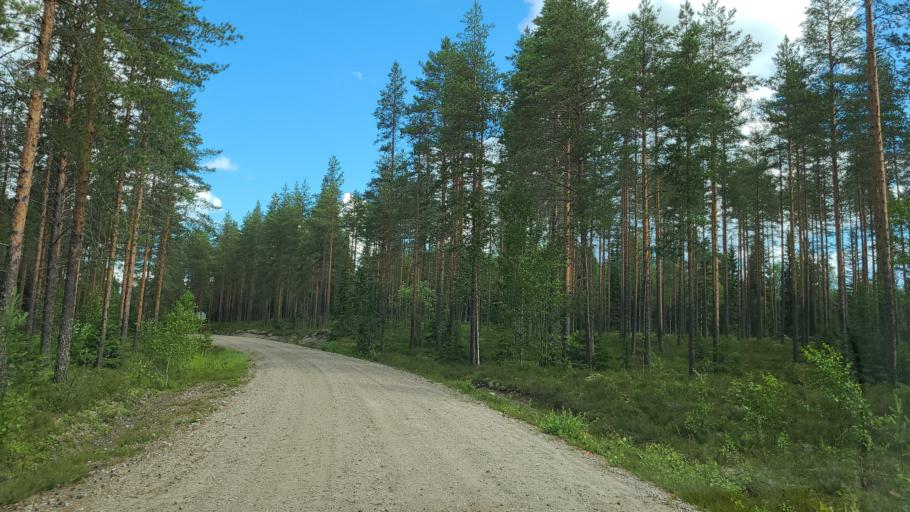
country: FI
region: Northern Savo
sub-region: Koillis-Savo
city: Kaavi
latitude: 63.0592
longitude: 28.8264
